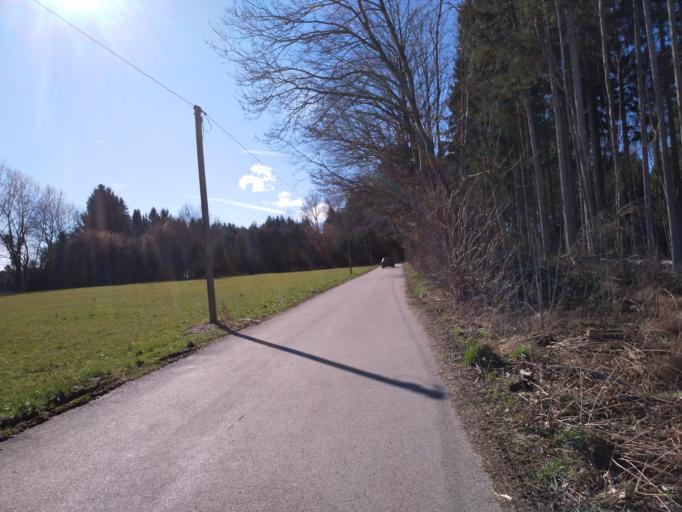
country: DE
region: Bavaria
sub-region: Swabia
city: Bad Worishofen
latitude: 47.9972
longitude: 10.5790
